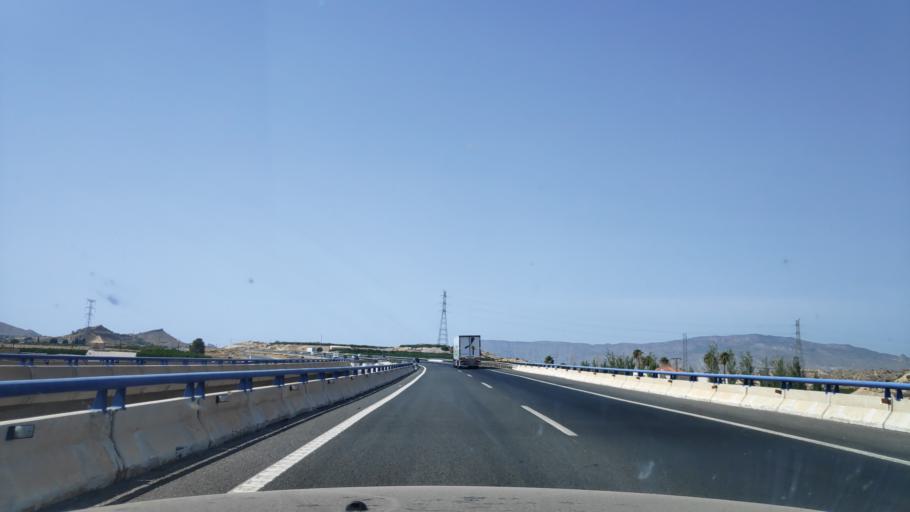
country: ES
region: Murcia
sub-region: Murcia
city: Archena
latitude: 38.1422
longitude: -1.2737
